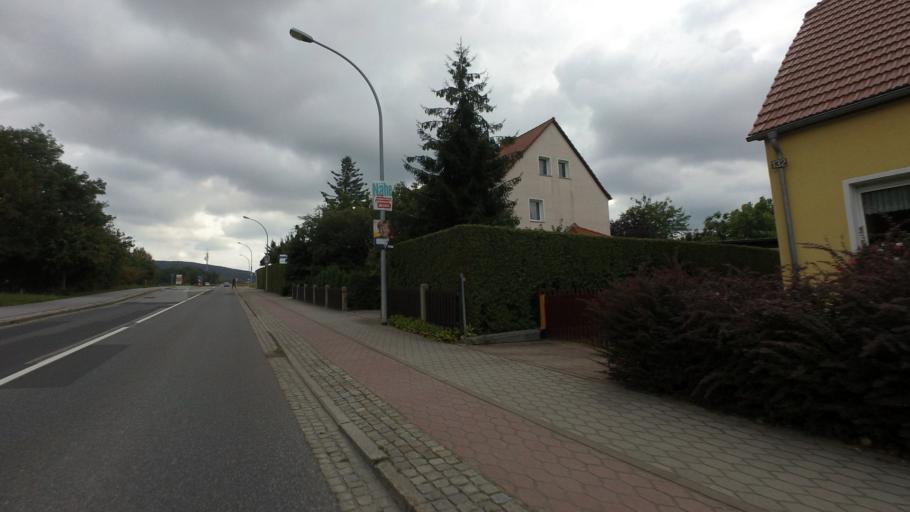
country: DE
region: Saxony
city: Bautzen
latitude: 51.1553
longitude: 14.4328
